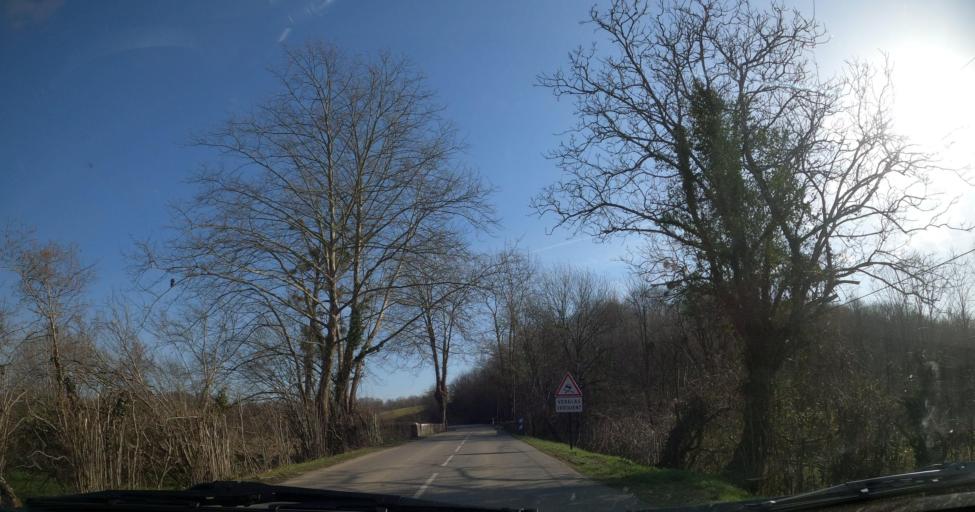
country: FR
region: Aquitaine
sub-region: Departement des Pyrenees-Atlantiques
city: Lahonce
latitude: 43.4518
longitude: -1.3767
